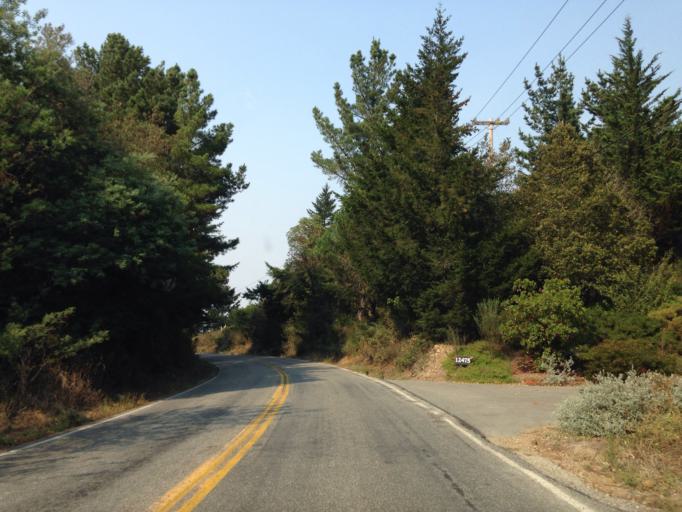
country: US
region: California
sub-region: San Mateo County
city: Highlands-Baywood Park
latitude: 37.4630
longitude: -122.3459
